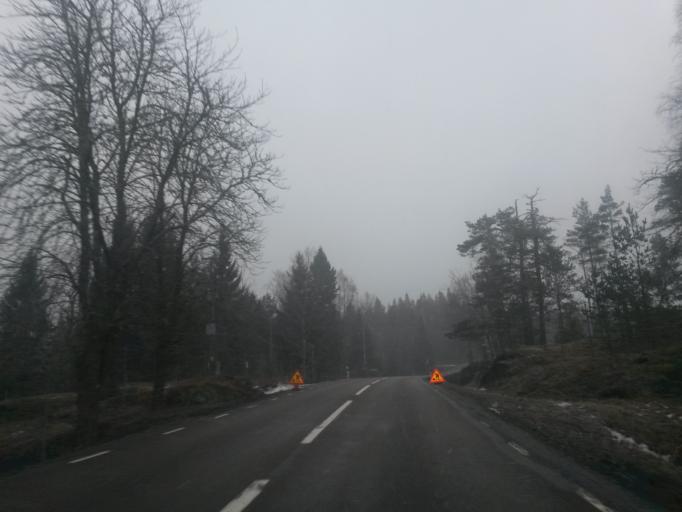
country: SE
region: Vaestra Goetaland
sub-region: Alingsas Kommun
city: Sollebrunn
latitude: 58.2005
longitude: 12.4307
